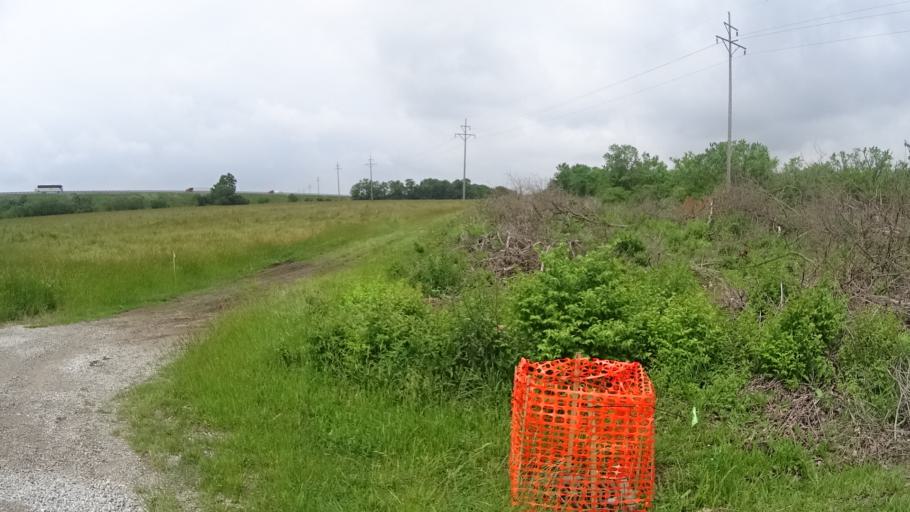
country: US
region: Ohio
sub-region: Huron County
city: Bellevue
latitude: 41.3466
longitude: -82.7855
